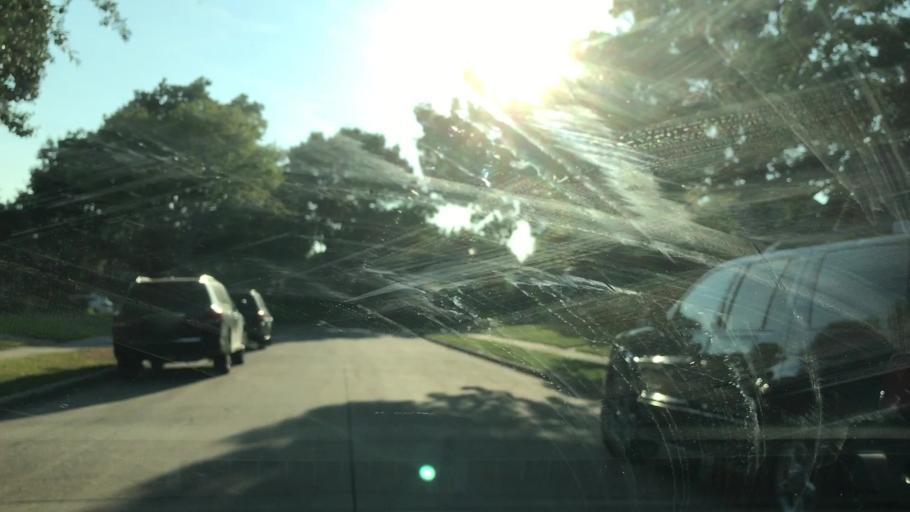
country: US
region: Texas
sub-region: Dallas County
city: Coppell
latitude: 32.9644
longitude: -96.9956
